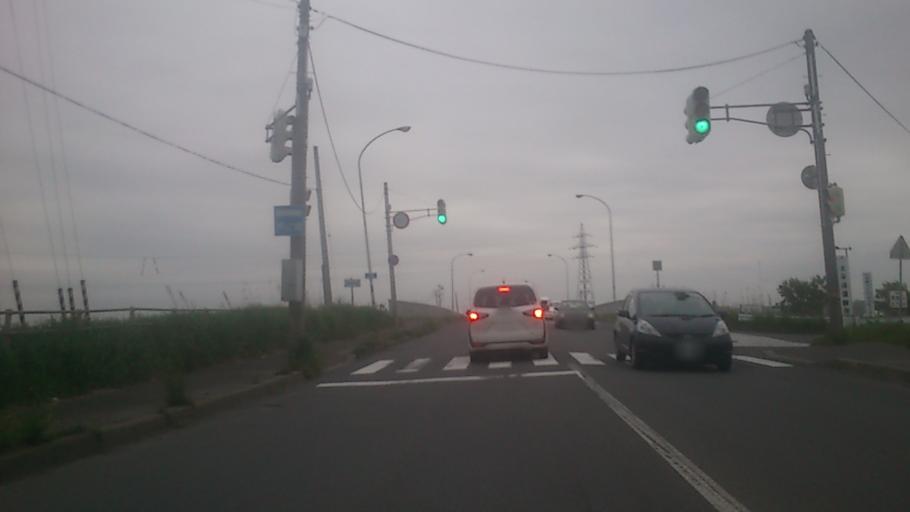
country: JP
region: Hokkaido
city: Kushiro
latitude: 42.9994
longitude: 144.4138
